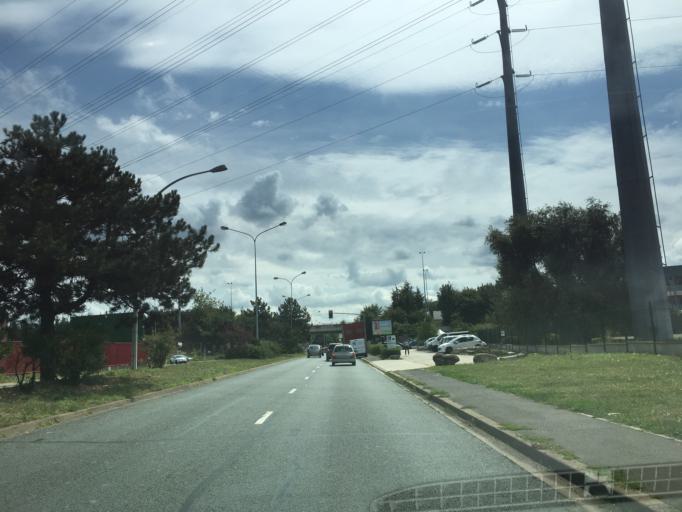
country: FR
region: Ile-de-France
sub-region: Departement du Val-de-Marne
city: Bonneuil-sur-Marne
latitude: 48.7596
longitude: 2.4802
